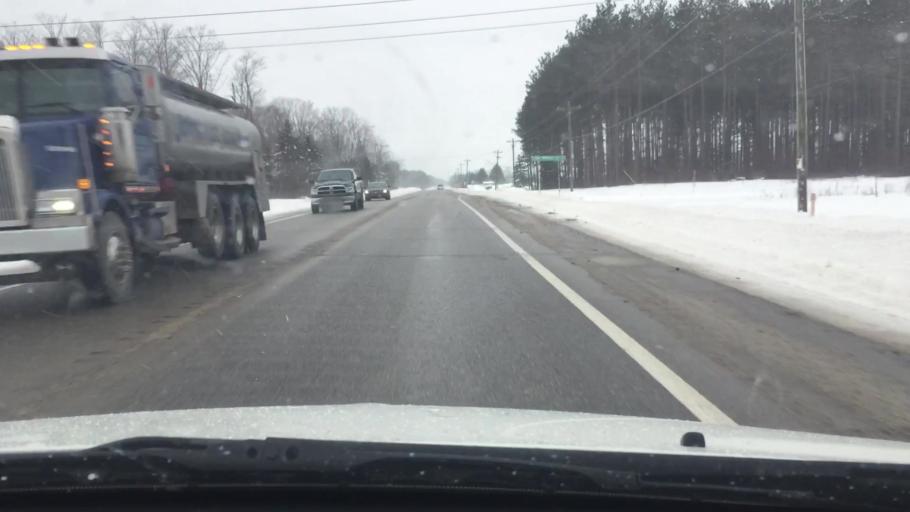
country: US
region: Michigan
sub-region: Otsego County
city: Gaylord
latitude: 45.0276
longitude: -84.7326
